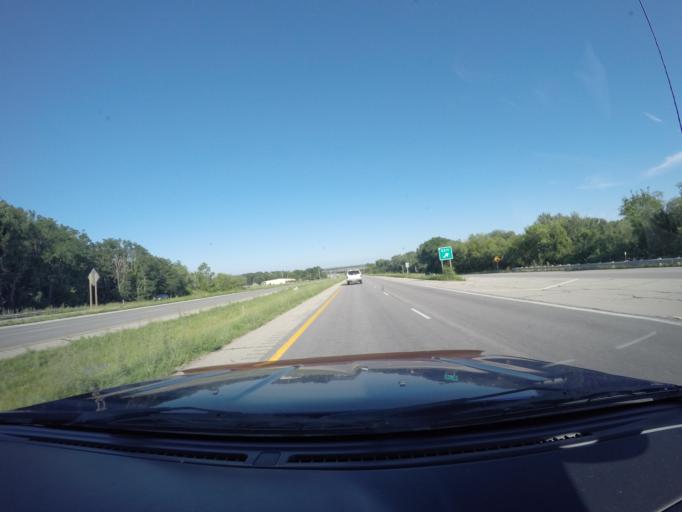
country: US
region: Kansas
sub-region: Shawnee County
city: Topeka
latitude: 39.0920
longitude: -95.5992
